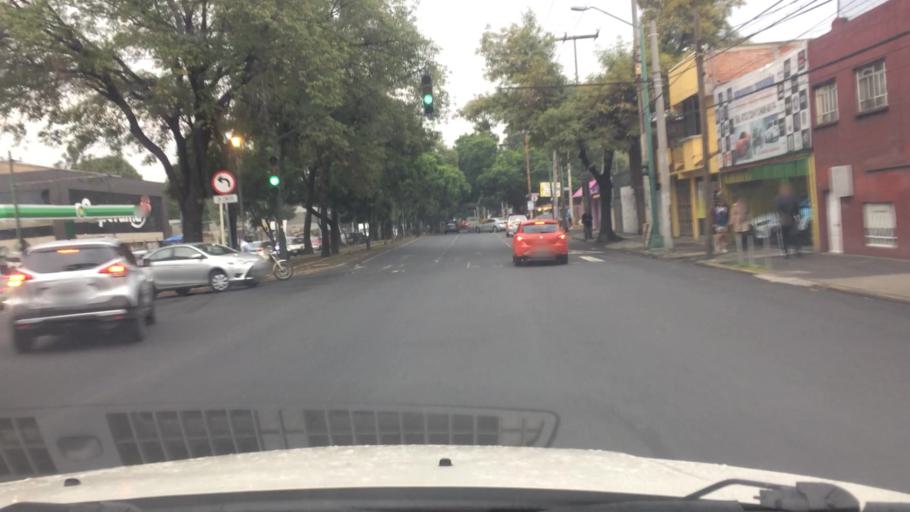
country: MX
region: Mexico City
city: Coyoacan
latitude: 19.3388
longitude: -99.1279
